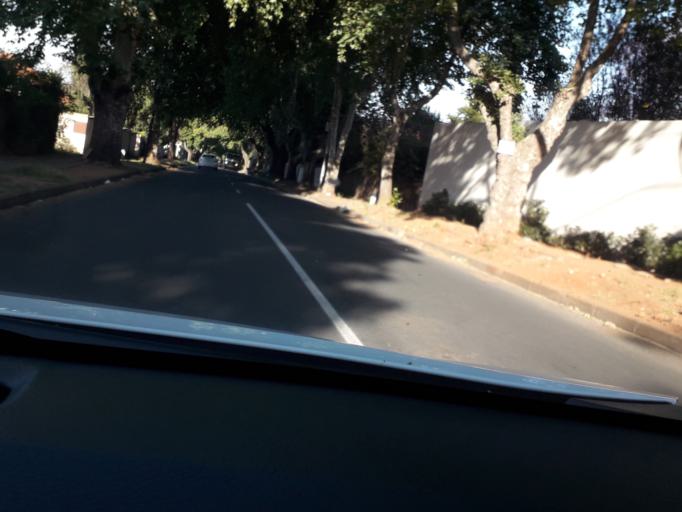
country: ZA
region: Gauteng
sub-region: City of Johannesburg Metropolitan Municipality
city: Johannesburg
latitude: -26.1446
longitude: 28.0847
